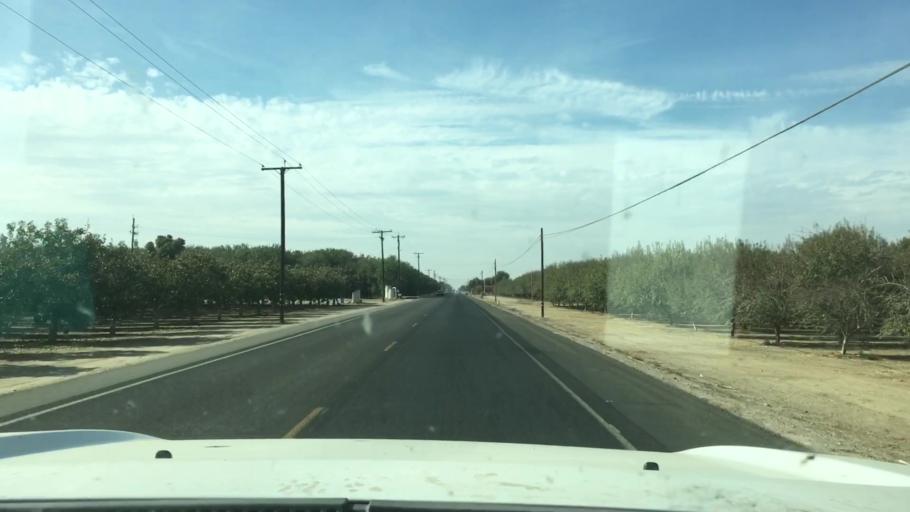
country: US
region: California
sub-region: Kern County
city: Shafter
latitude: 35.4999
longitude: -119.3033
